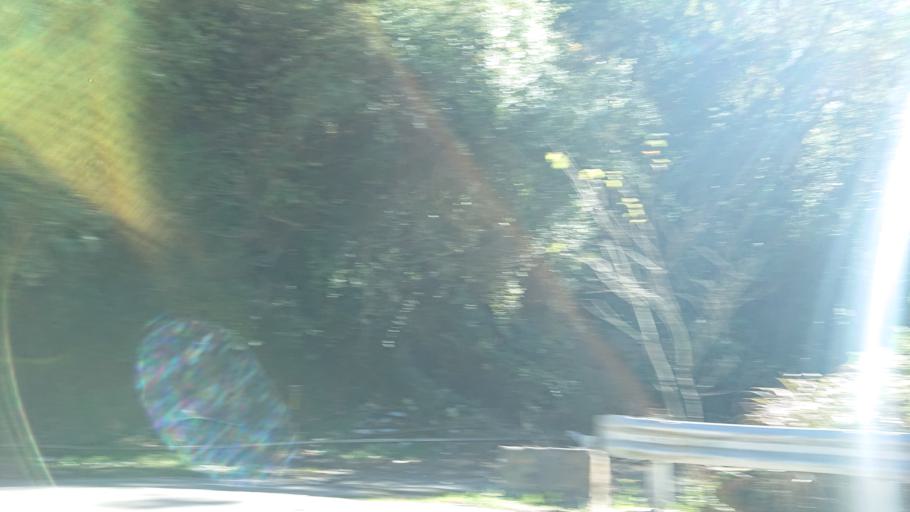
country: TW
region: Taiwan
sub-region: Hualien
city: Hualian
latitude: 24.3491
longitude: 121.3255
